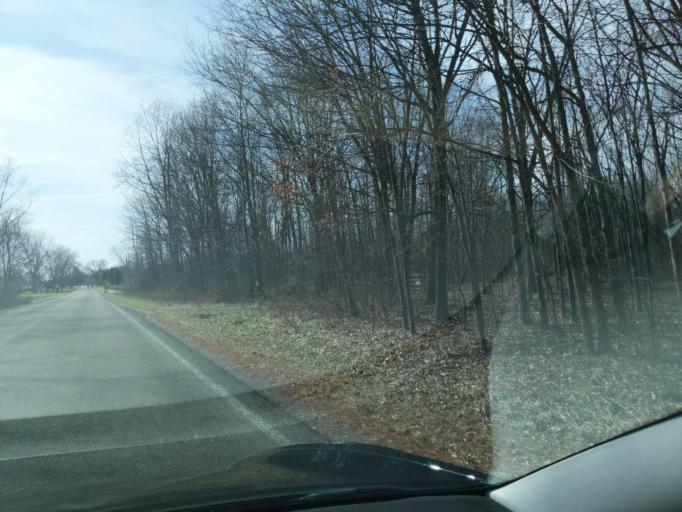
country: US
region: Michigan
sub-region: Ingham County
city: Stockbridge
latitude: 42.4831
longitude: -84.2615
